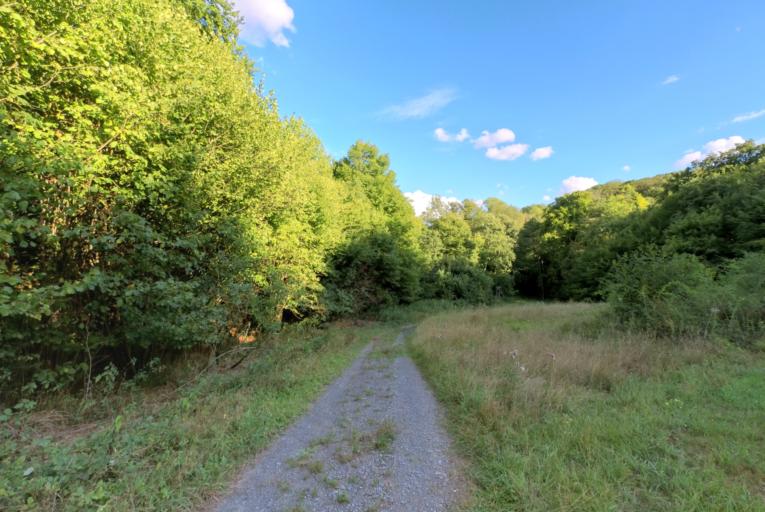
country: DE
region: Baden-Wuerttemberg
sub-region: Karlsruhe Region
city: Mosbach
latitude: 49.3397
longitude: 9.1649
